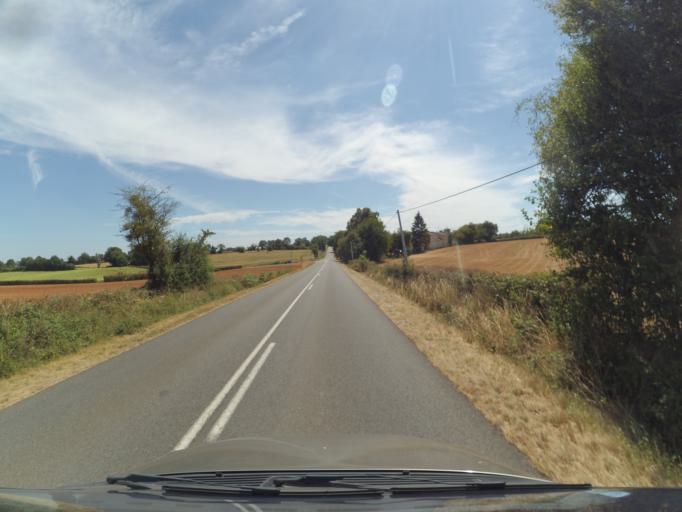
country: FR
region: Poitou-Charentes
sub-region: Departement de la Vienne
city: Usson-du-Poitou
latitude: 46.2037
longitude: 0.5343
